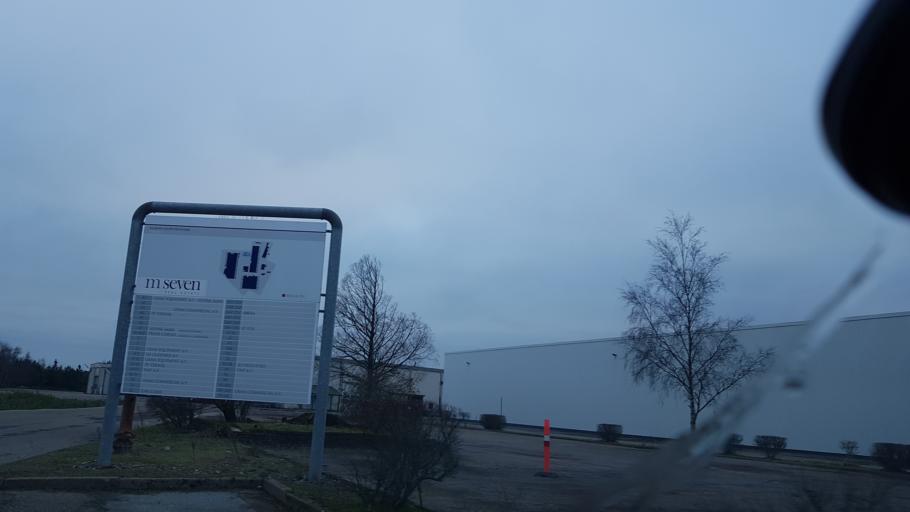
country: DK
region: South Denmark
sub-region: Haderslev Kommune
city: Vojens
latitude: 55.2429
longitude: 9.3026
